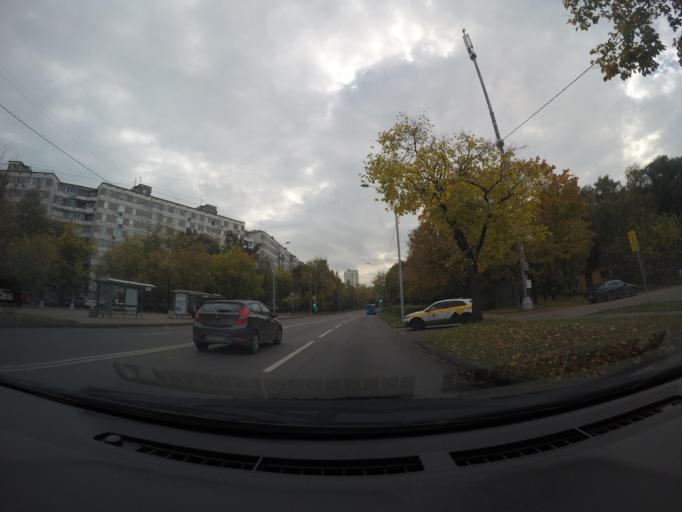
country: RU
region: Moscow
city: Ivanovskoye
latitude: 55.7653
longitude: 37.8224
